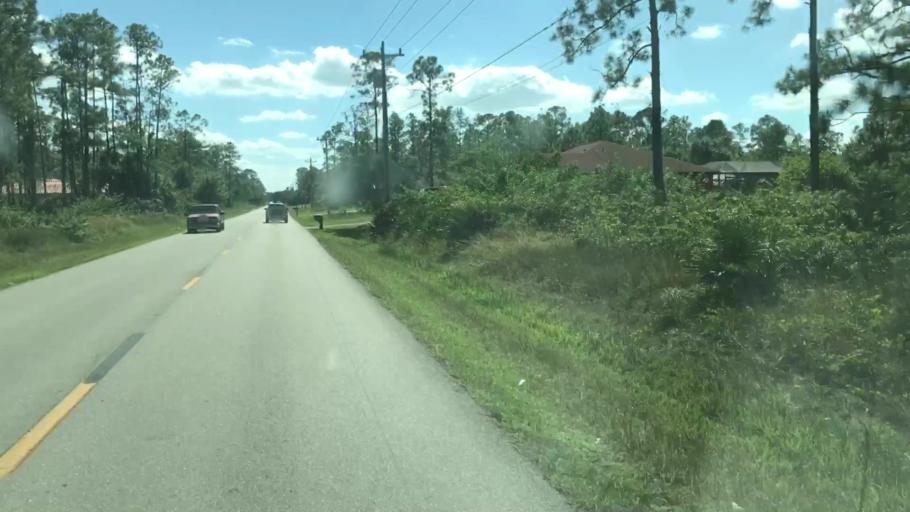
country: US
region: Florida
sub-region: Lee County
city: Lehigh Acres
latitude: 26.6337
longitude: -81.6466
